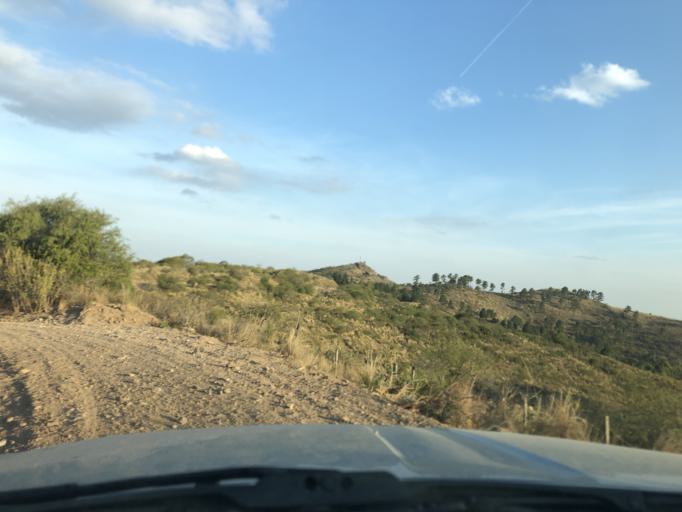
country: AR
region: Cordoba
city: Agua de Oro
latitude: -31.0579
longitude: -64.3509
